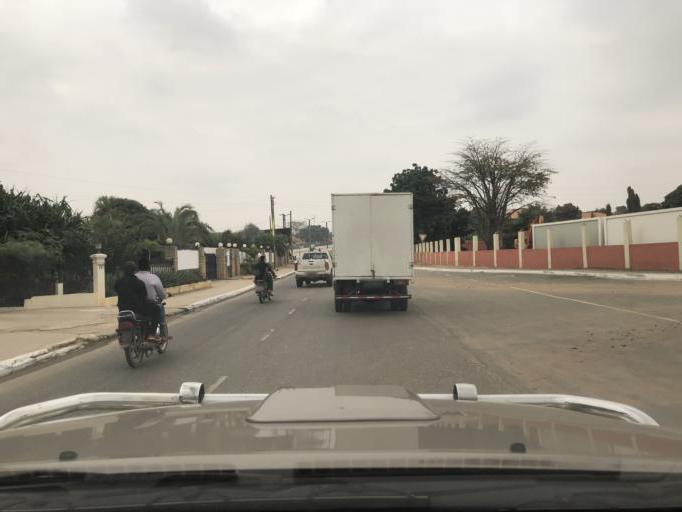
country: AO
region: Luanda
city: Luanda
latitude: -8.9082
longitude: 13.1661
